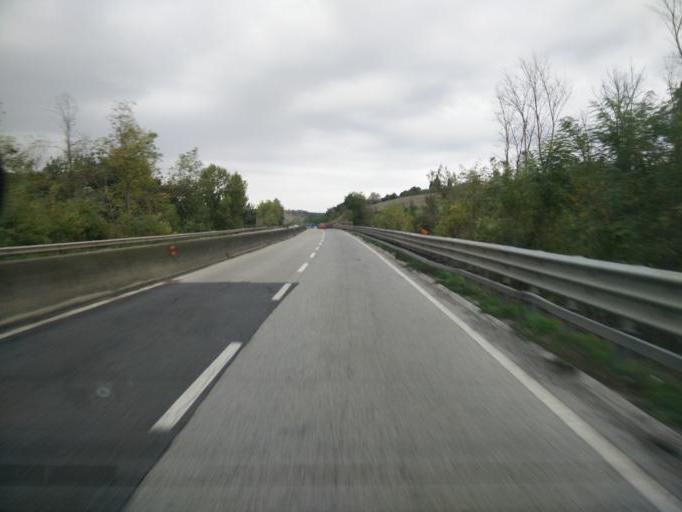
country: IT
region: Tuscany
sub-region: Provincia di Siena
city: Belverde
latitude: 43.3264
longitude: 11.2962
